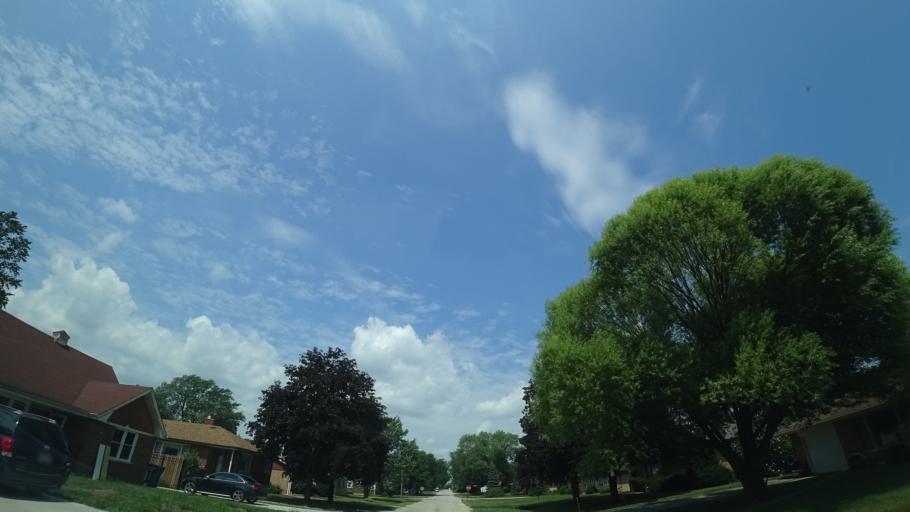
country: US
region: Illinois
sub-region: Cook County
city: Worth
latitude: 41.6840
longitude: -87.7835
